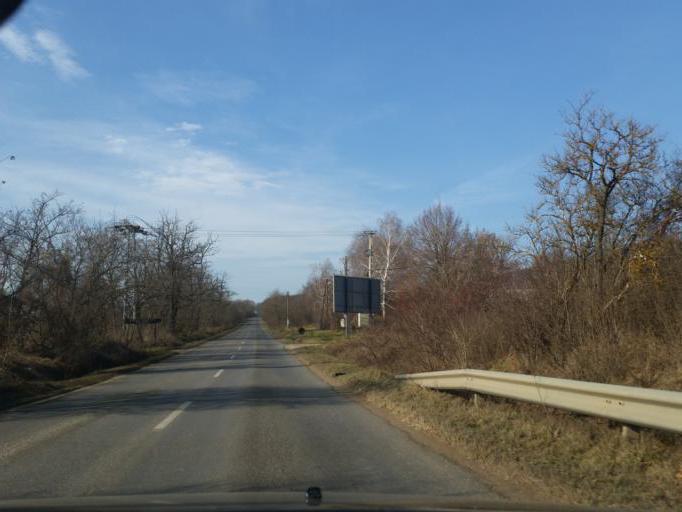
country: HU
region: Pest
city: Budakeszi
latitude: 47.5199
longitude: 18.9098
